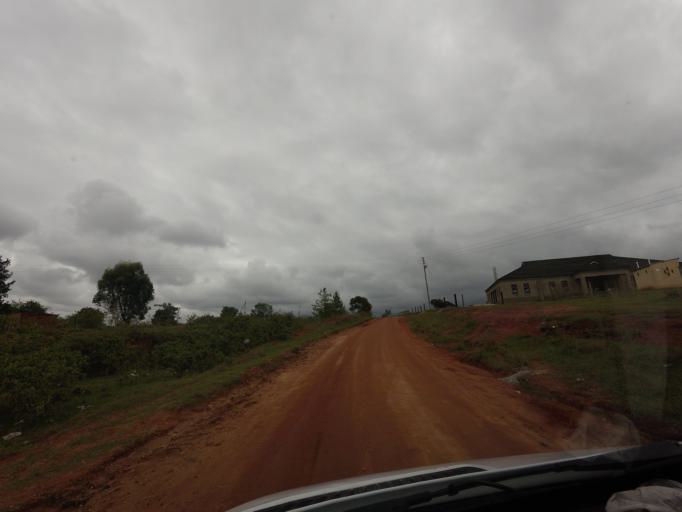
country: SZ
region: Hhohho
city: Lobamba
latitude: -26.4783
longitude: 31.1999
